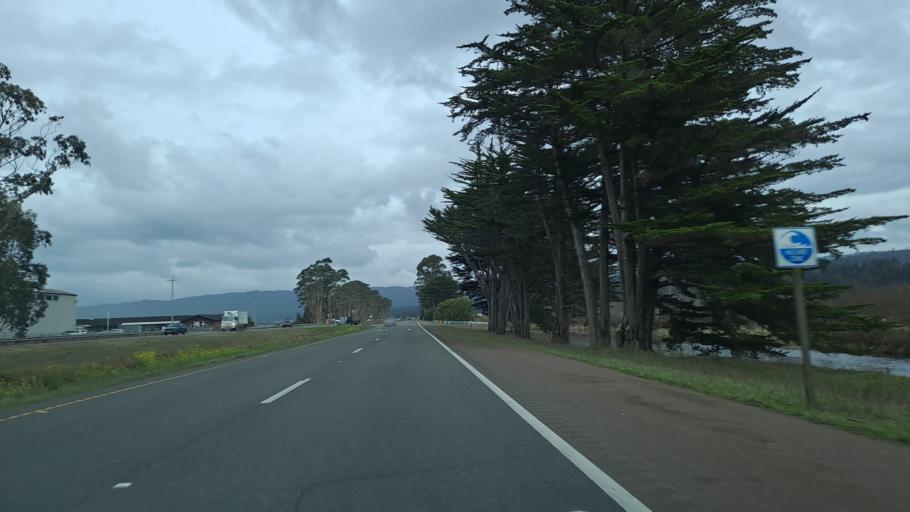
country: US
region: California
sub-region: Humboldt County
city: Myrtletown
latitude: 40.8127
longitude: -124.1079
